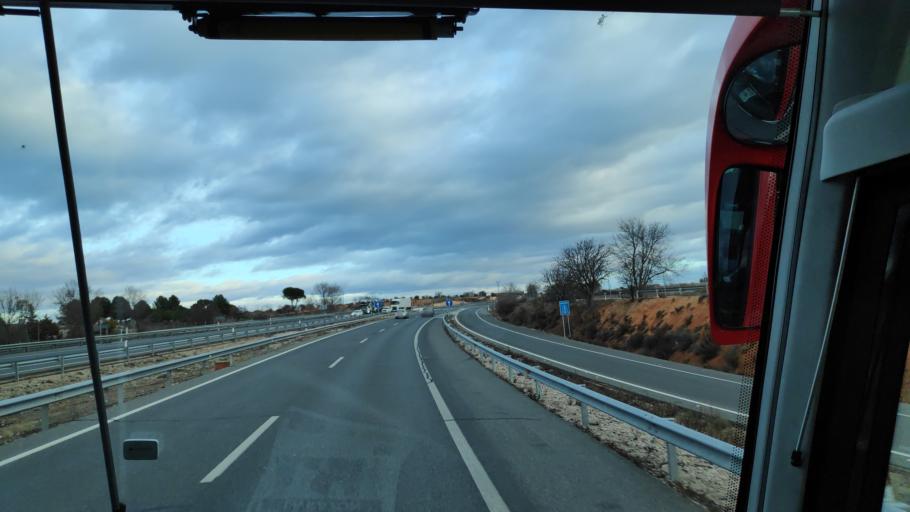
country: ES
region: Madrid
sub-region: Provincia de Madrid
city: Villarejo de Salvanes
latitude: 40.1626
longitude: -3.2667
